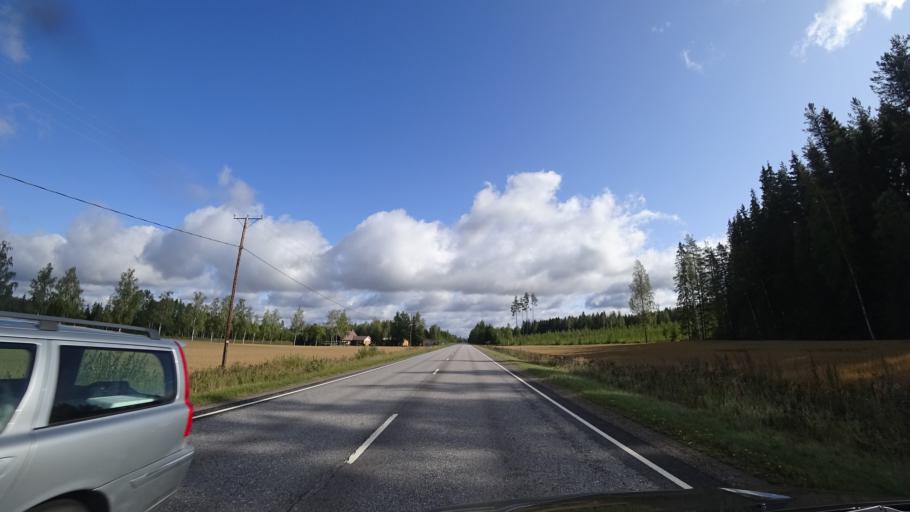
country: FI
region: Uusimaa
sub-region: Helsinki
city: Hyvinge
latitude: 60.5414
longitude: 24.9300
